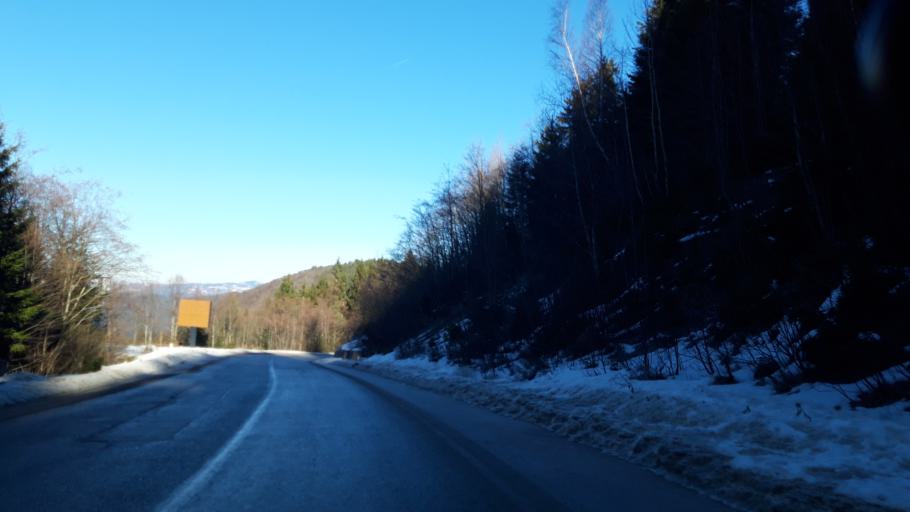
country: BA
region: Republika Srpska
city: Koran
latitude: 43.7816
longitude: 18.5532
